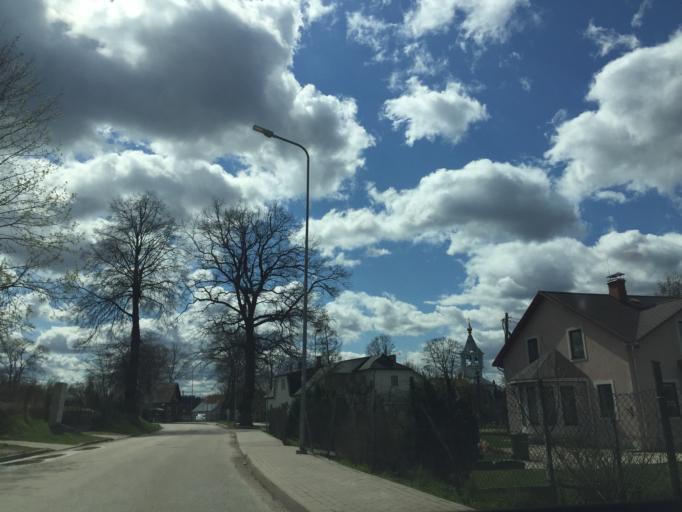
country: LV
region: Rezekne
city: Rezekne
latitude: 56.4911
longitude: 27.3415
